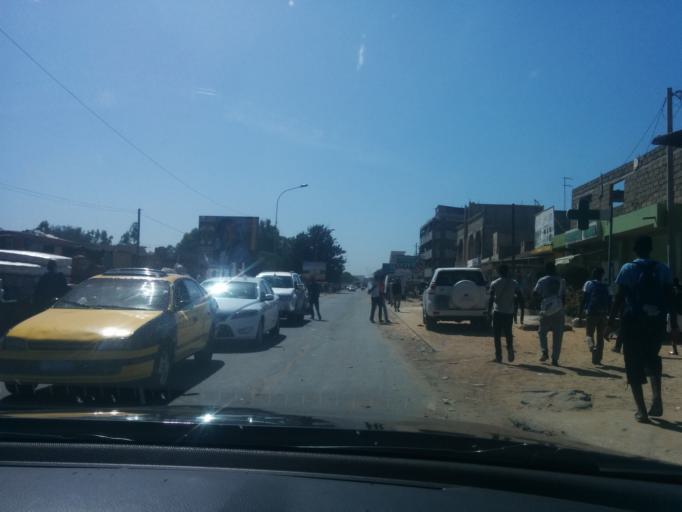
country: SN
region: Dakar
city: Grand Dakar
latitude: 14.7351
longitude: -17.4461
